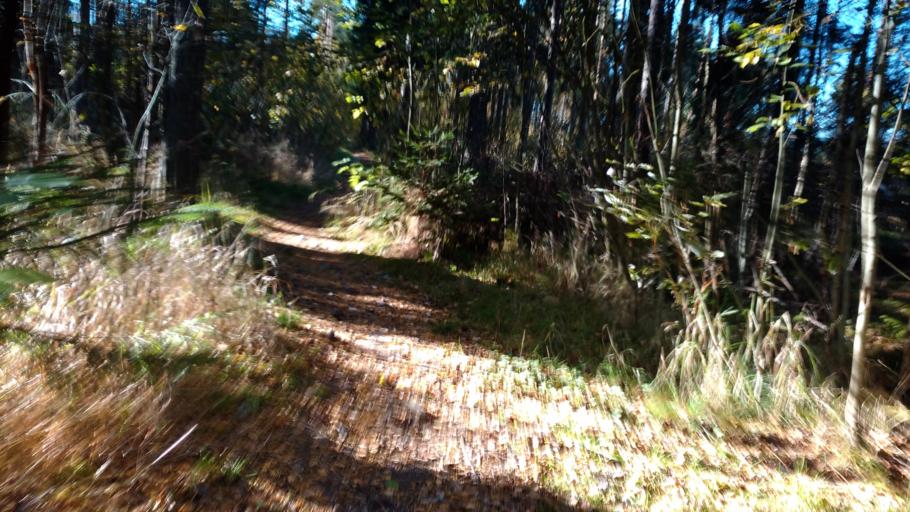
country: FI
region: Varsinais-Suomi
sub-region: Salo
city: Salo
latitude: 60.4047
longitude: 23.1879
